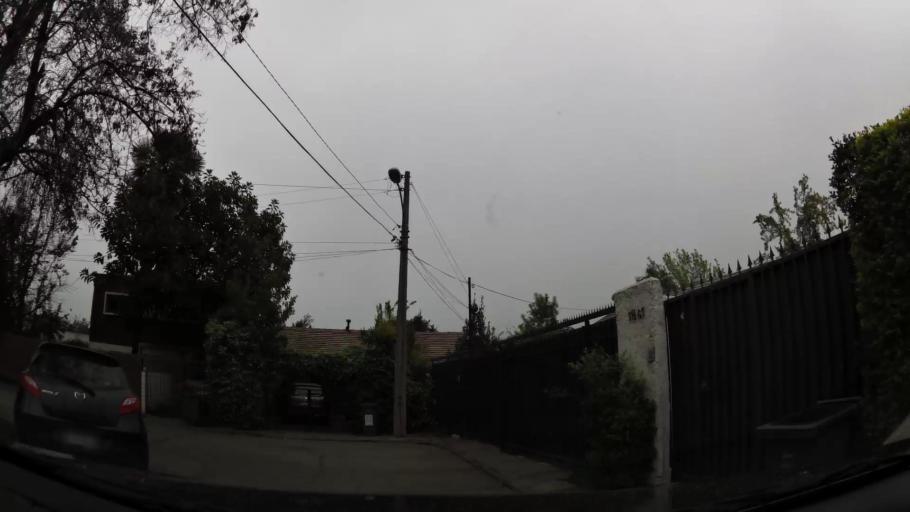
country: CL
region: Santiago Metropolitan
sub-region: Provincia de Santiago
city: Villa Presidente Frei, Nunoa, Santiago, Chile
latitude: -33.3835
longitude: -70.5557
